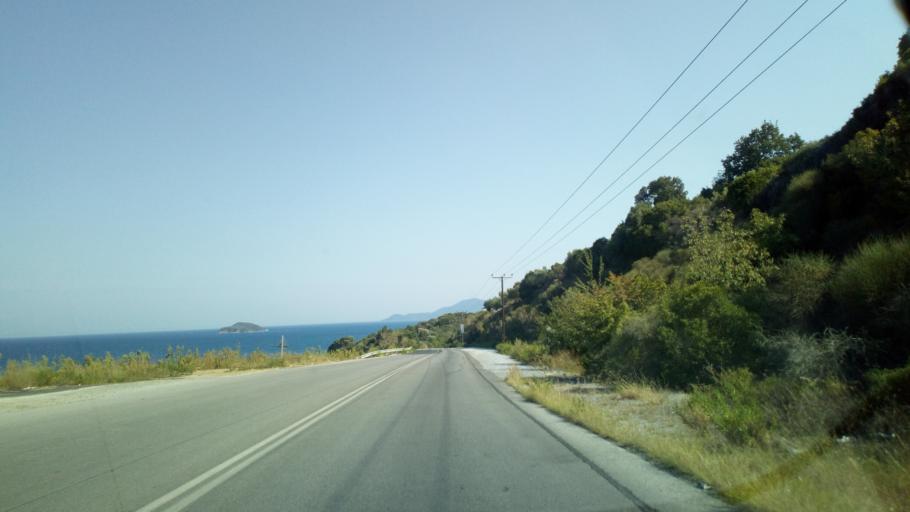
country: GR
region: Central Macedonia
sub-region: Nomos Thessalonikis
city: Stavros
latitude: 40.6325
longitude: 23.7615
